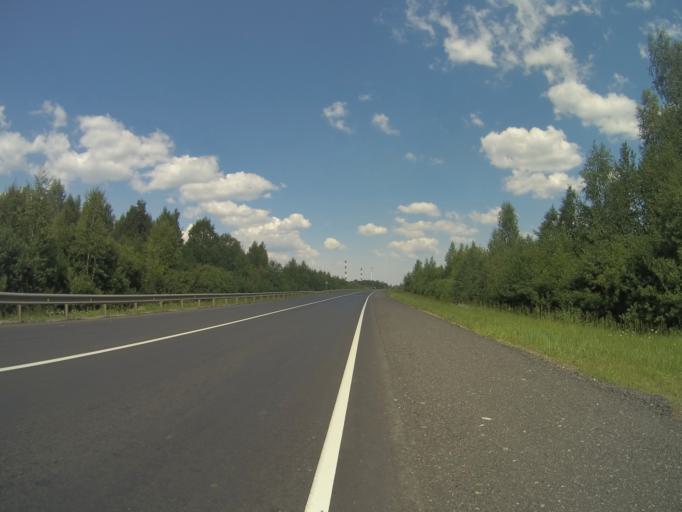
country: RU
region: Kostroma
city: Volgorechensk
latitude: 57.4208
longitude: 41.1916
